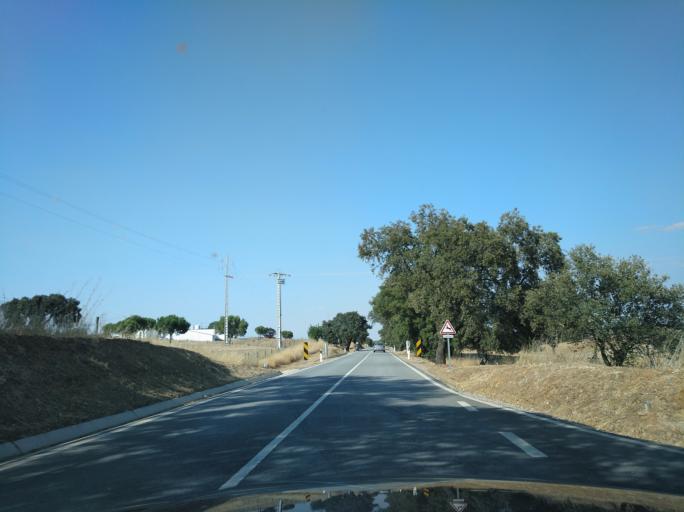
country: ES
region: Andalusia
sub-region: Provincia de Huelva
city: Rosal de la Frontera
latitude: 37.9887
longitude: -7.2925
